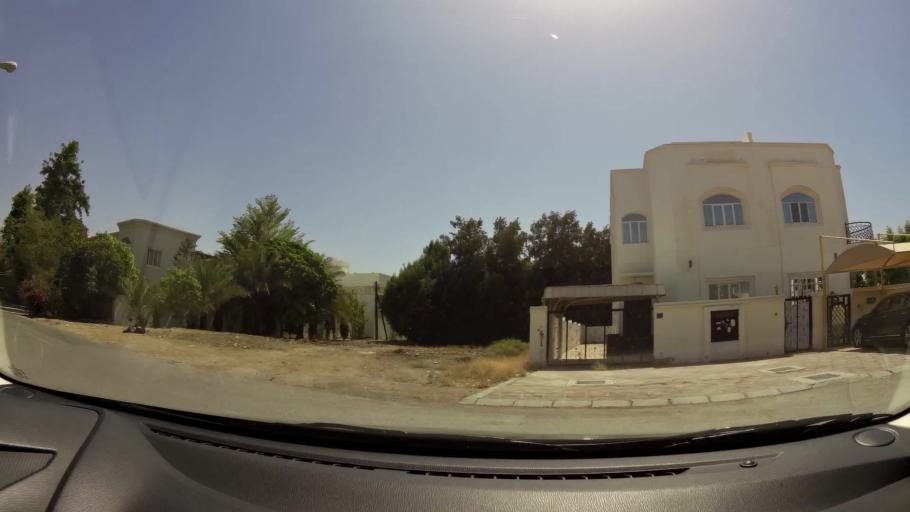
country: OM
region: Muhafazat Masqat
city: Bawshar
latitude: 23.6005
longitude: 58.3563
